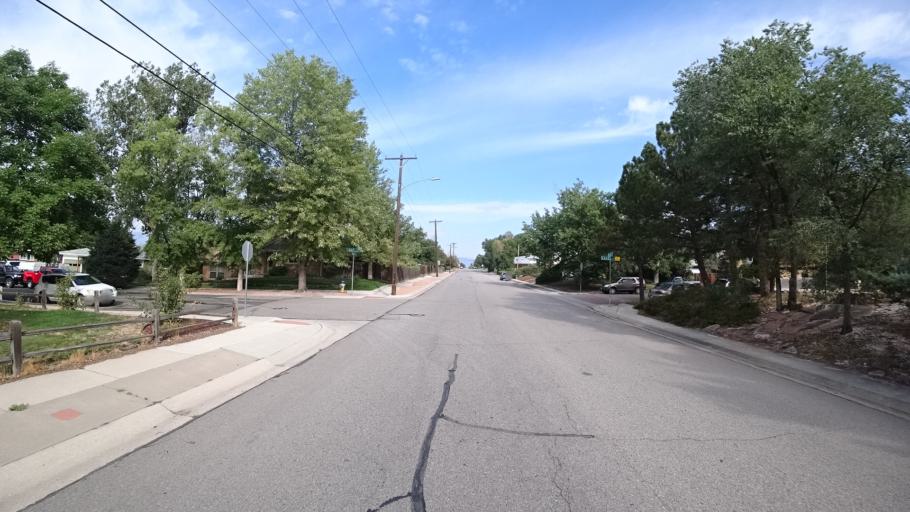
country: US
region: Colorado
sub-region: El Paso County
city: Colorado Springs
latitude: 38.8846
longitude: -104.7963
